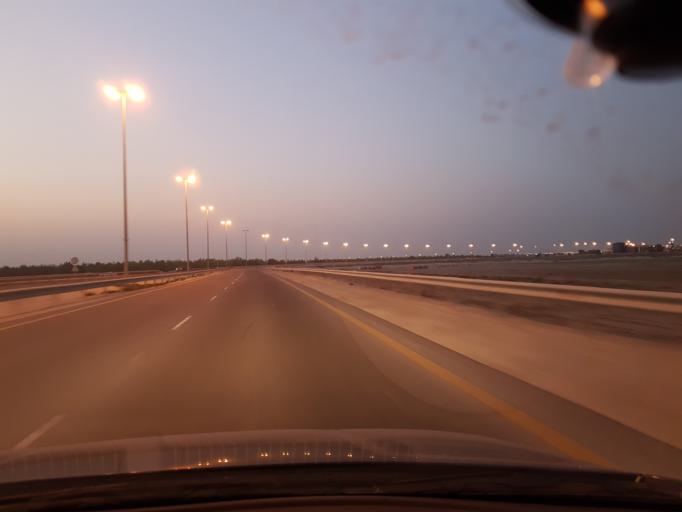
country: BH
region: Central Governorate
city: Dar Kulayb
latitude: 26.0091
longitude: 50.4843
